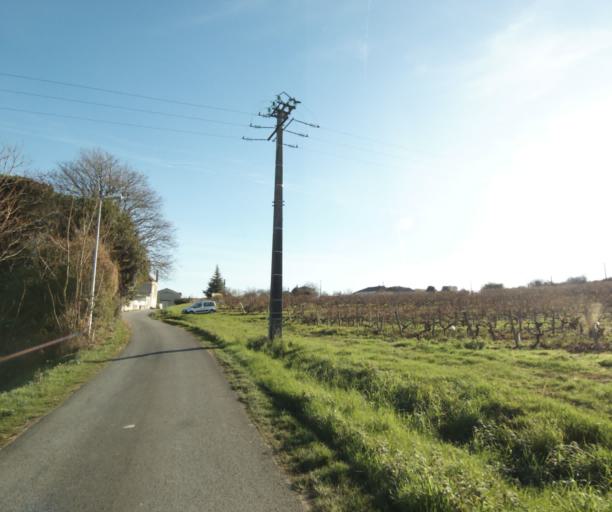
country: FR
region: Poitou-Charentes
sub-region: Departement de la Charente-Maritime
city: Burie
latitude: 45.7724
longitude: -0.4263
